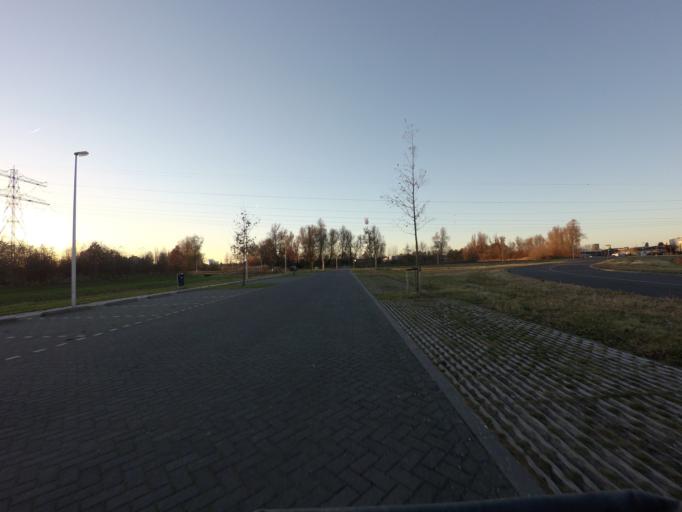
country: NL
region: Utrecht
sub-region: Gemeente Nieuwegein
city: Nieuwegein
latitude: 52.0767
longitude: 5.0626
